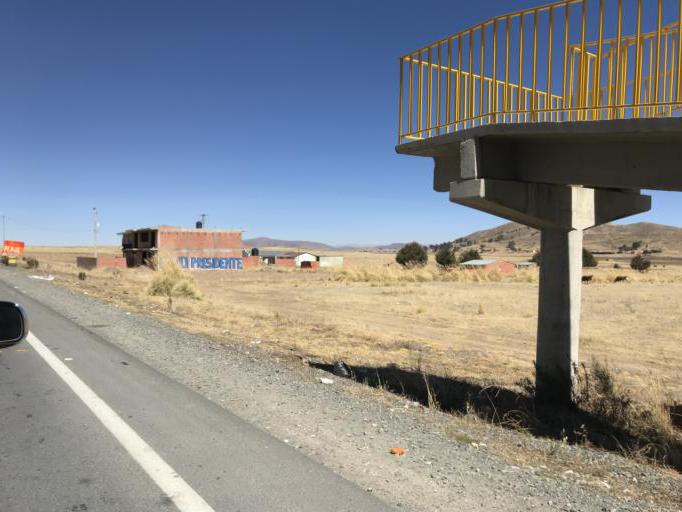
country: BO
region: La Paz
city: Huarina
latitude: -16.2209
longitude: -68.5861
